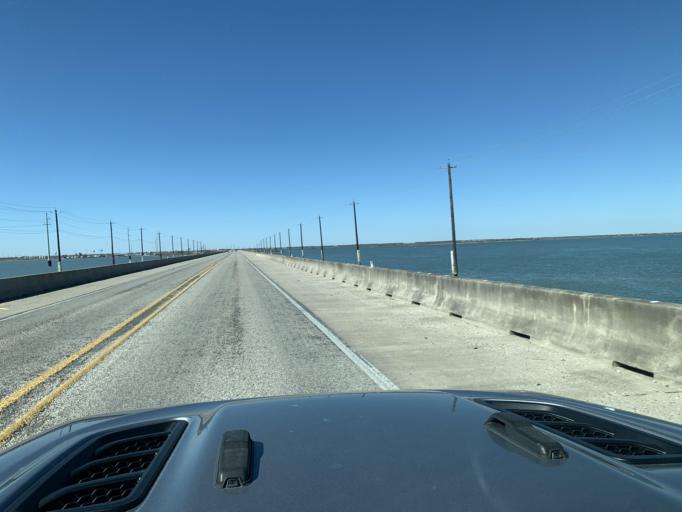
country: US
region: Texas
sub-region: San Patricio County
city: Aransas Pass
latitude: 27.8822
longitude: -97.1021
